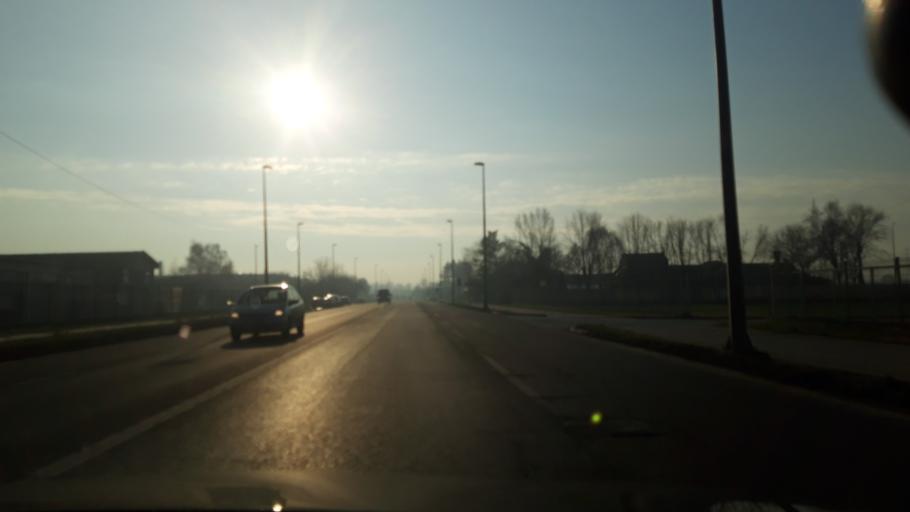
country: RS
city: Pocerski Pricinovic
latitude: 44.7450
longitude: 19.7200
